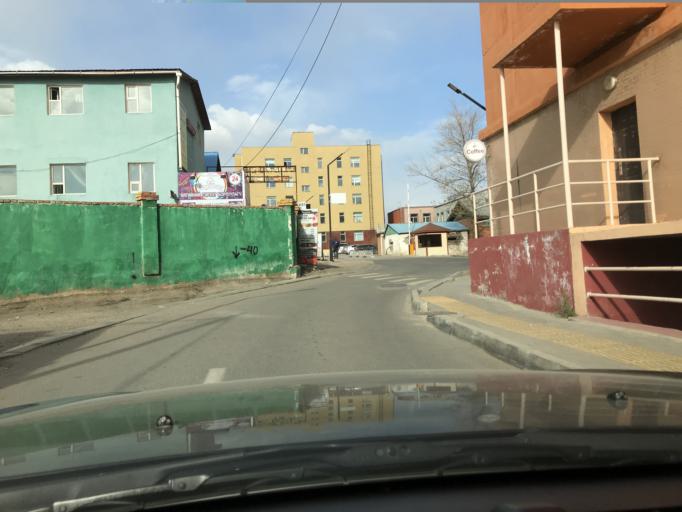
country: MN
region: Ulaanbaatar
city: Ulaanbaatar
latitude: 47.9147
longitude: 106.9674
